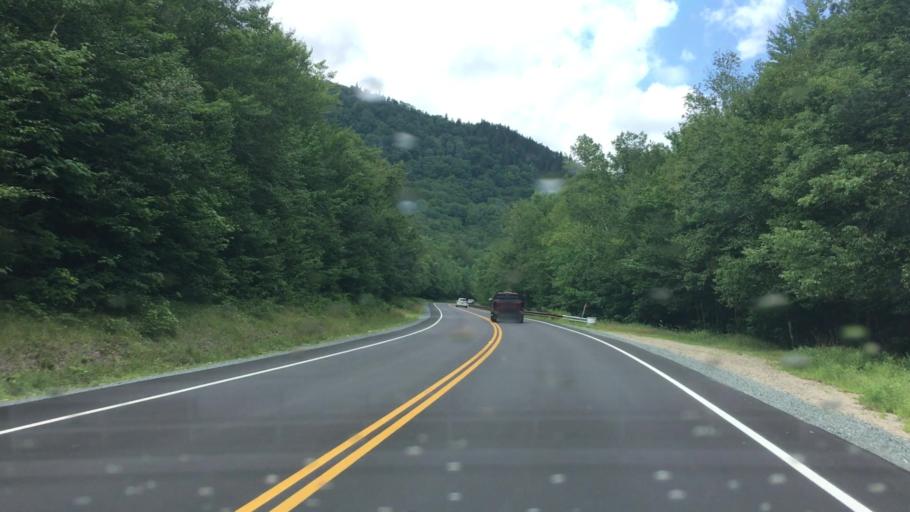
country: US
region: New Hampshire
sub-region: Grafton County
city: Woodstock
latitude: 44.0270
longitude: -71.7566
